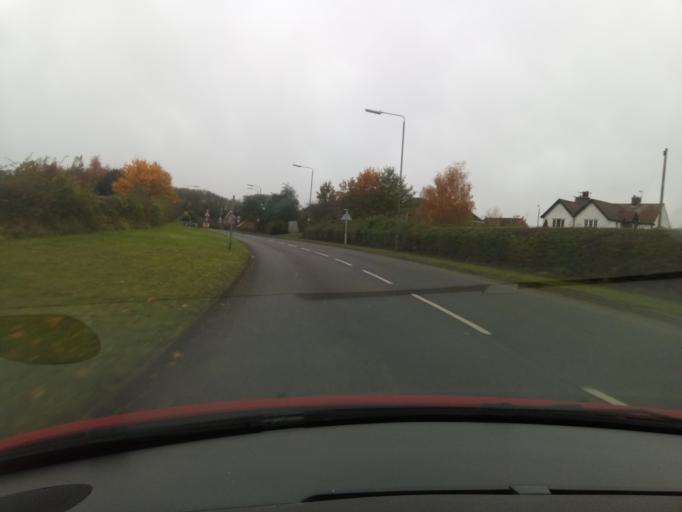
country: GB
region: England
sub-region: Derbyshire
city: Melbourne
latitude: 52.8738
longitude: -1.4245
